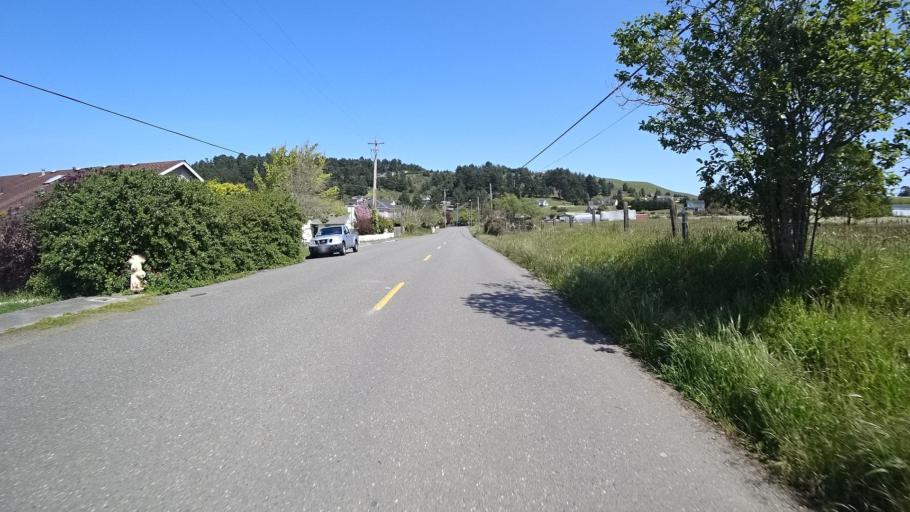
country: US
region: California
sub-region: Humboldt County
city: Hydesville
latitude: 40.5629
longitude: -124.1291
